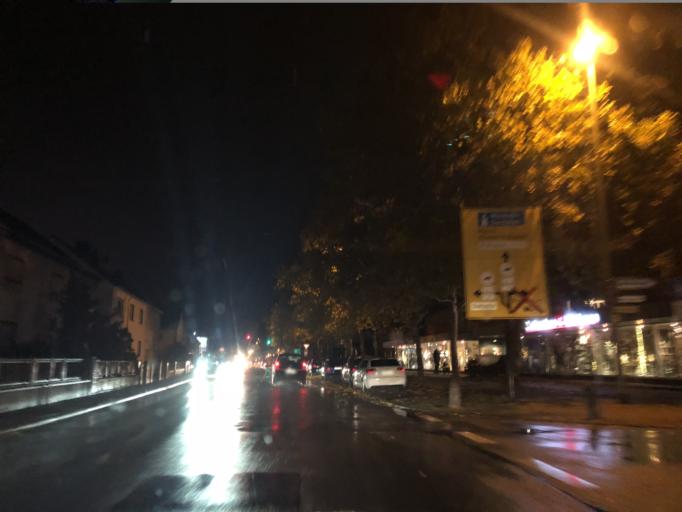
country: DE
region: Hesse
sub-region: Regierungsbezirk Darmstadt
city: Hochheim am Main
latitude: 50.0123
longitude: 8.3610
